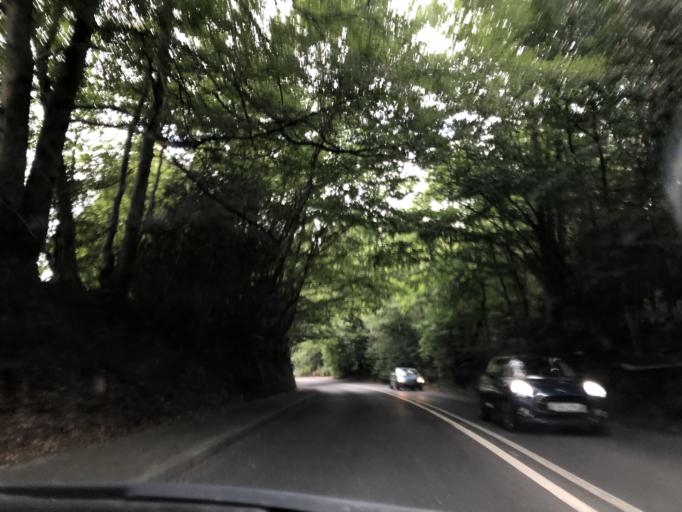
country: GB
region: England
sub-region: Kent
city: Sevenoaks
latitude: 51.2568
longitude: 0.1992
